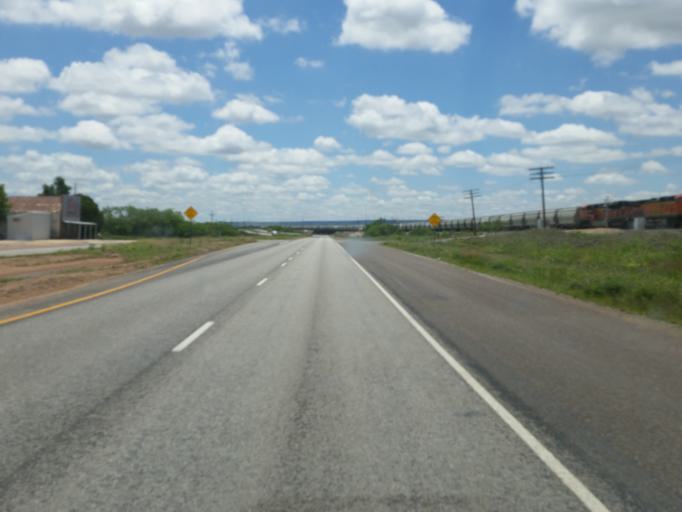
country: US
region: Texas
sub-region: Garza County
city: Post
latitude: 33.0436
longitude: -101.2036
